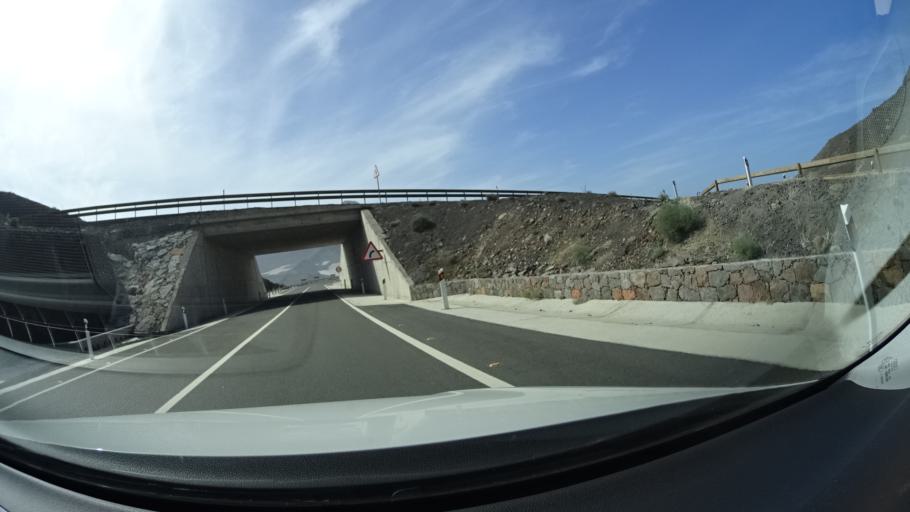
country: ES
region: Canary Islands
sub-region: Provincia de Las Palmas
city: San Nicolas
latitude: 28.0098
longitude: -15.7874
